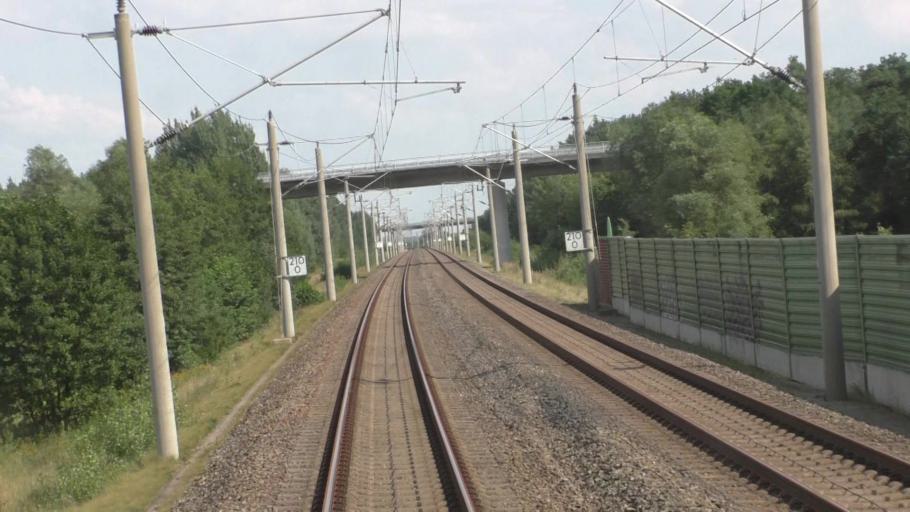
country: DE
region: Saxony-Anhalt
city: Uenglingen
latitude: 52.5795
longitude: 11.7917
